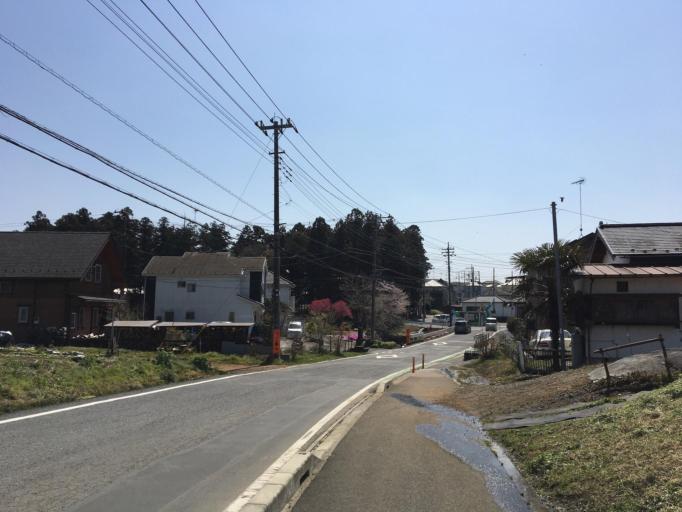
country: JP
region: Saitama
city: Sayama
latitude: 35.8965
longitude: 139.3667
